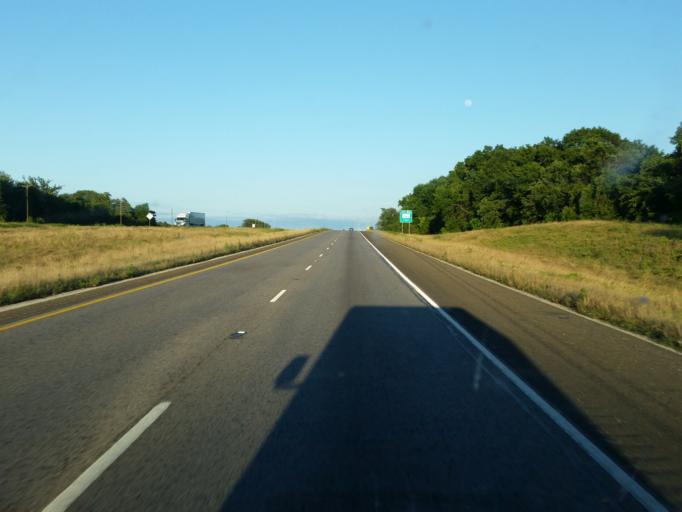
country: US
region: Texas
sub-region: Van Zandt County
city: Wills Point
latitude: 32.6606
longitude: -96.1153
